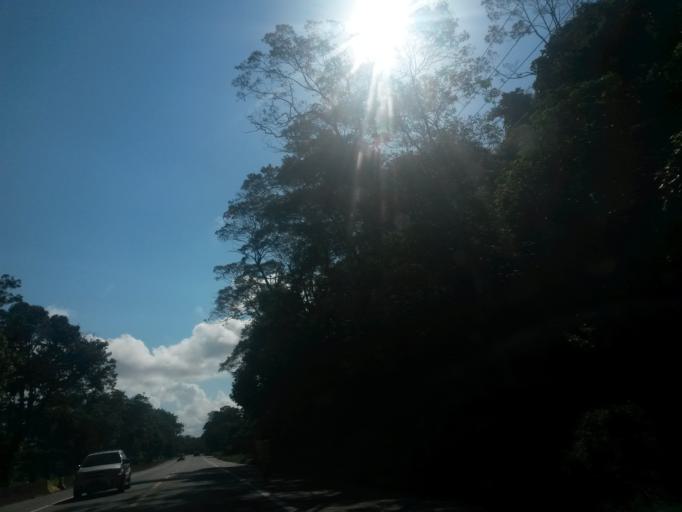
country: BR
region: Sao Paulo
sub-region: Sao Bernardo Do Campo
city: Sao Bernardo do Campo
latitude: -23.7786
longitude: -46.5144
